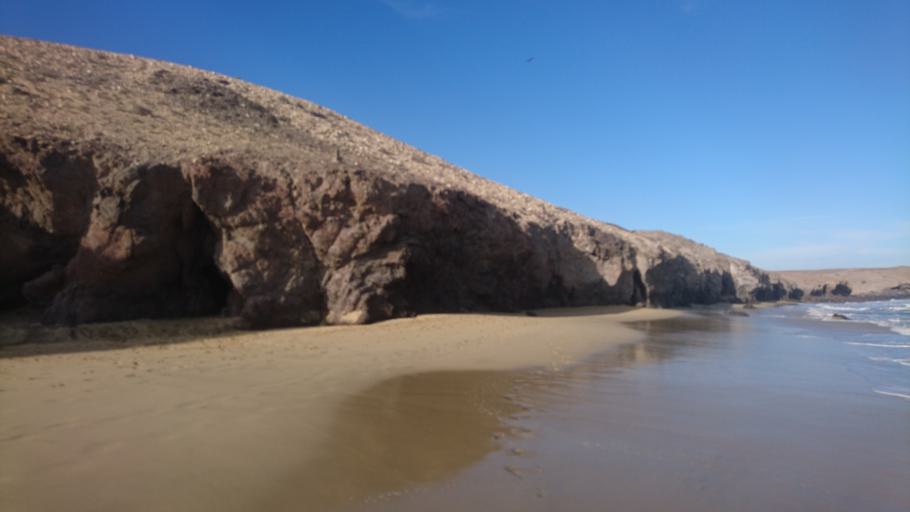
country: ES
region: Canary Islands
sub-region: Provincia de Las Palmas
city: Playa Blanca
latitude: 28.8423
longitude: -13.7845
